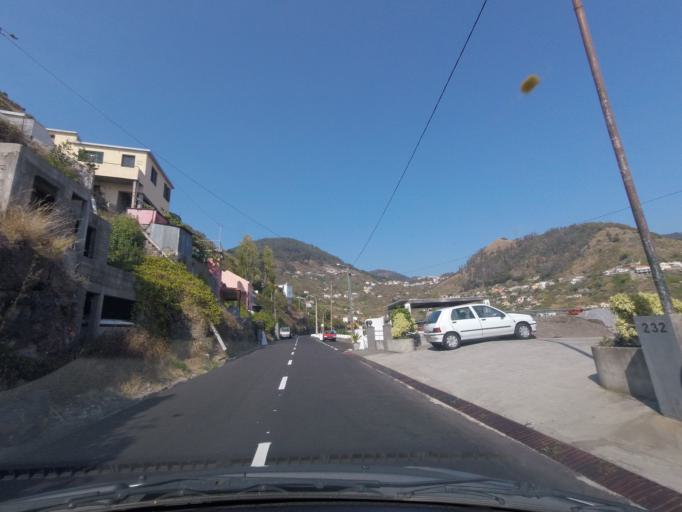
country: PT
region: Madeira
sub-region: Ribeira Brava
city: Campanario
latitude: 32.6697
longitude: -17.0445
